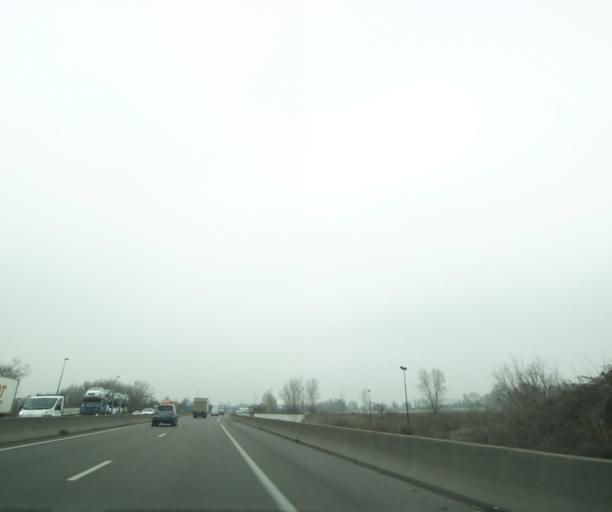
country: FR
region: Rhone-Alpes
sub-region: Departement du Rhone
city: Chassieu
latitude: 45.7496
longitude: 4.9871
